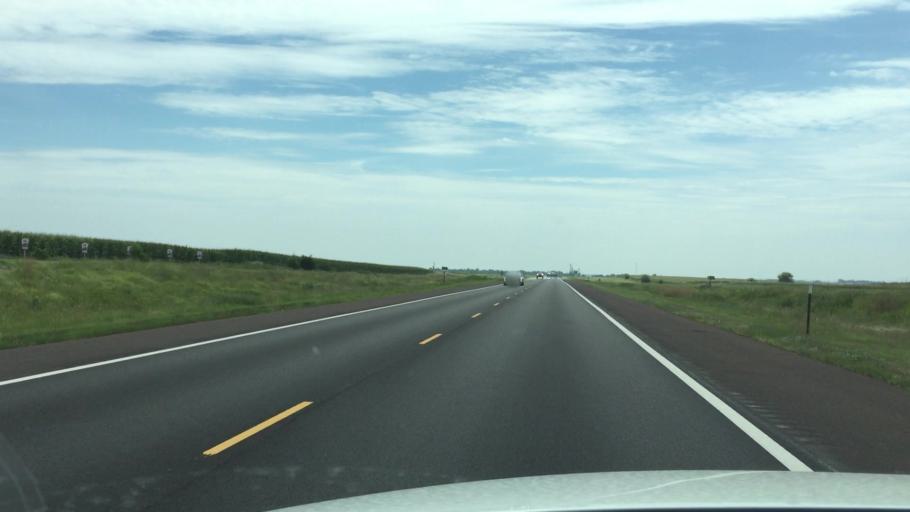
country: US
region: Kansas
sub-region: Nemaha County
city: Sabetha
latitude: 39.8556
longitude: -95.7547
